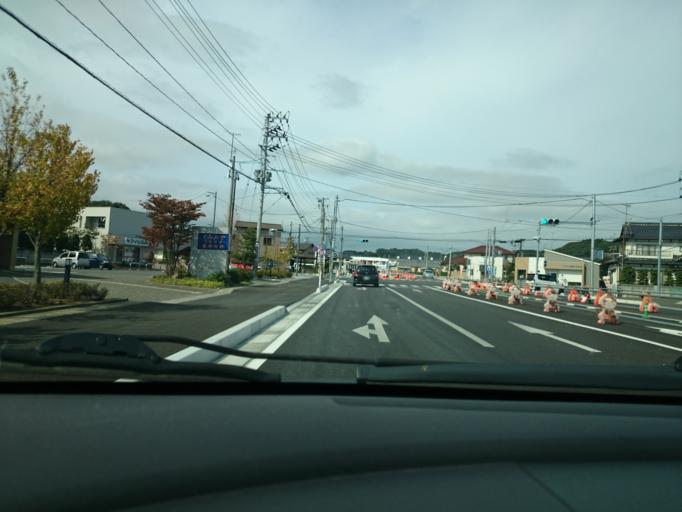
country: JP
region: Fukushima
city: Iwaki
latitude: 36.9776
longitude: 140.8883
